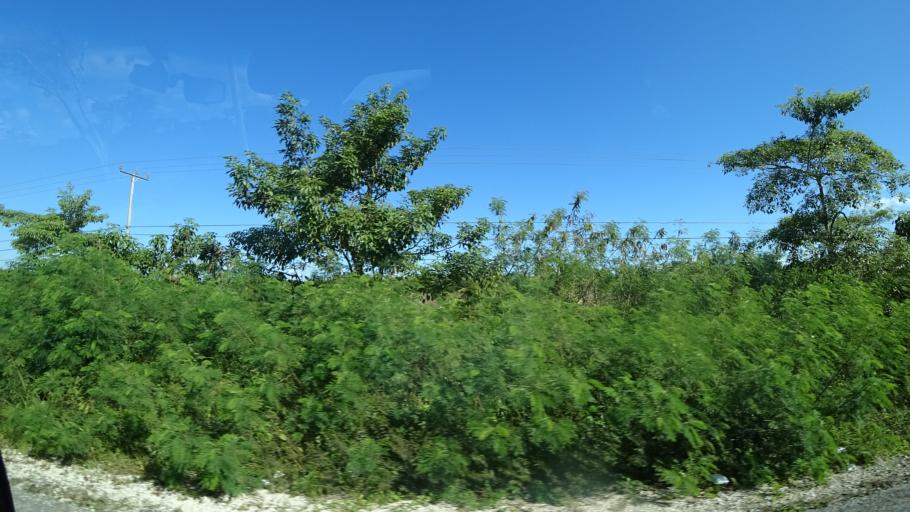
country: BZ
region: Belize
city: Belize City
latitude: 17.5455
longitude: -88.2743
